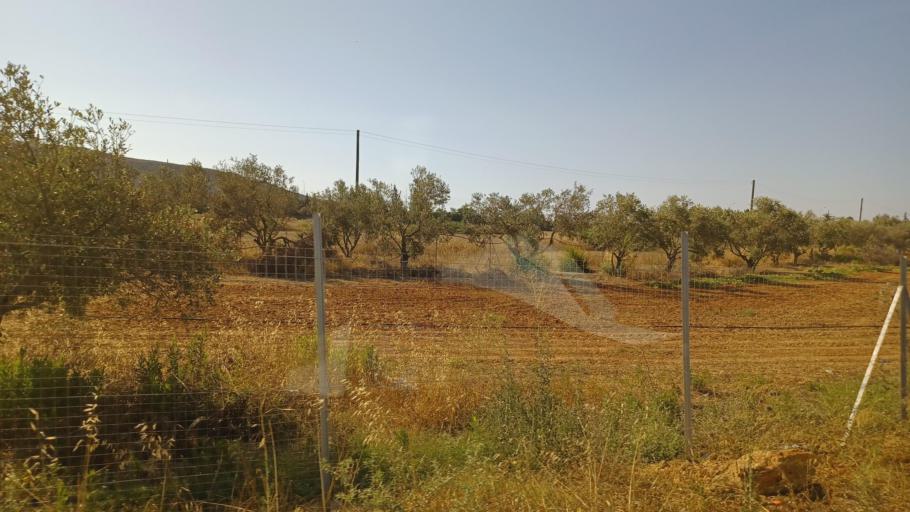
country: CY
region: Larnaka
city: Pyla
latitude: 34.9922
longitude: 33.6921
